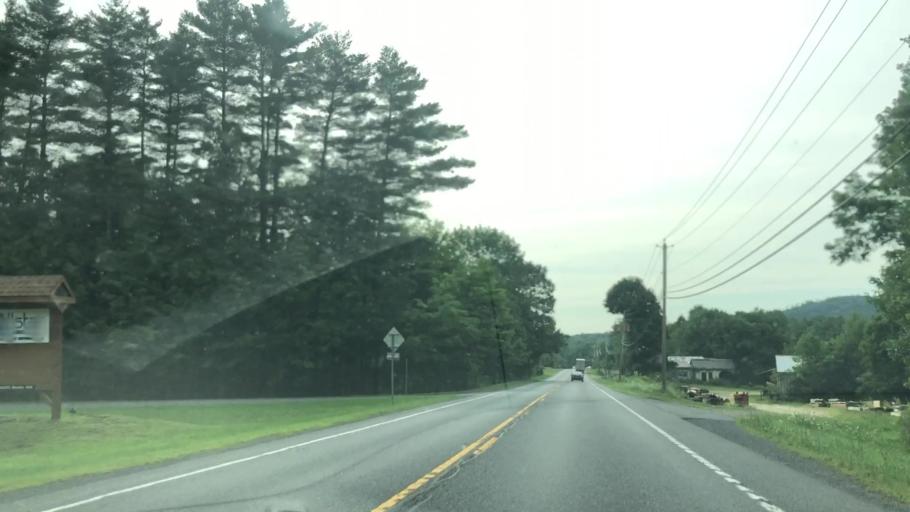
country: US
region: New York
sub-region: Warren County
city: Queensbury
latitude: 43.4035
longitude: -73.5893
